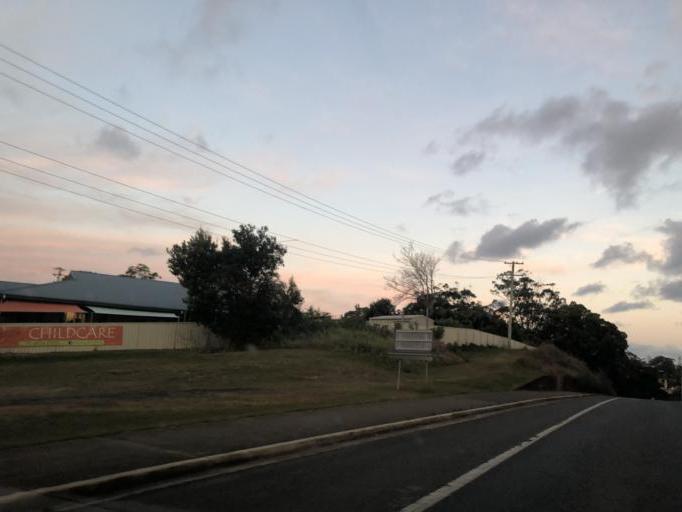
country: AU
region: New South Wales
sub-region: Coffs Harbour
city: Woolgoolga
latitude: -30.1073
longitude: 153.1892
